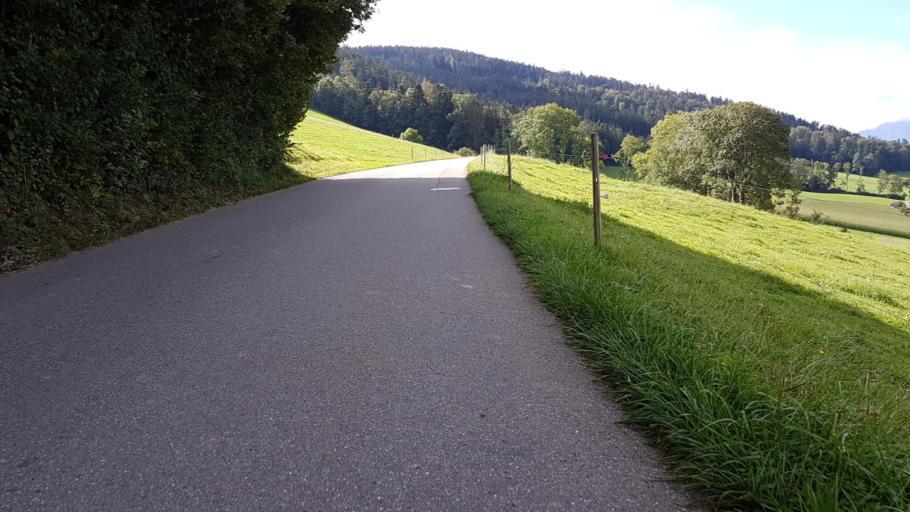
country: CH
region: Bern
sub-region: Bern-Mittelland District
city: Konolfingen
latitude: 46.8659
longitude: 7.6326
